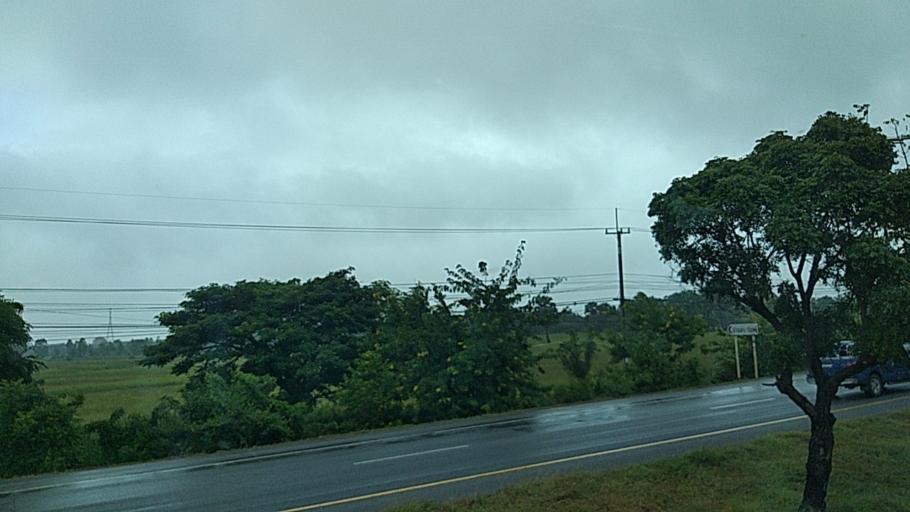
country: TH
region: Nakhon Ratchasima
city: Non Sung
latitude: 15.2074
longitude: 102.3552
